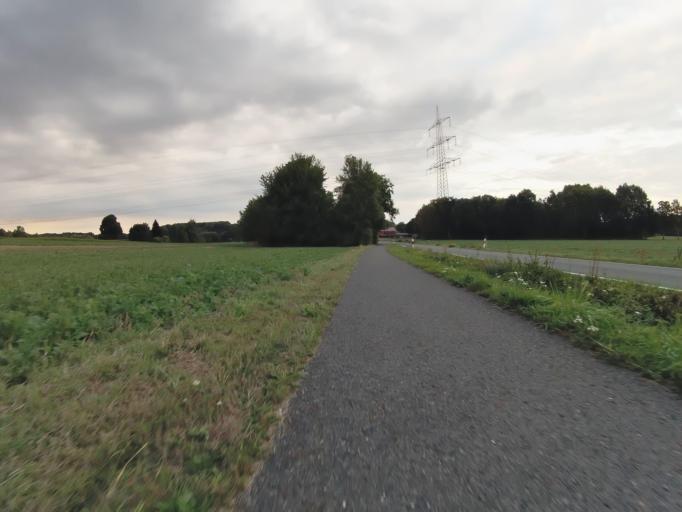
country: DE
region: North Rhine-Westphalia
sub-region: Regierungsbezirk Munster
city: Westerkappeln
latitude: 52.2754
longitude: 7.8635
